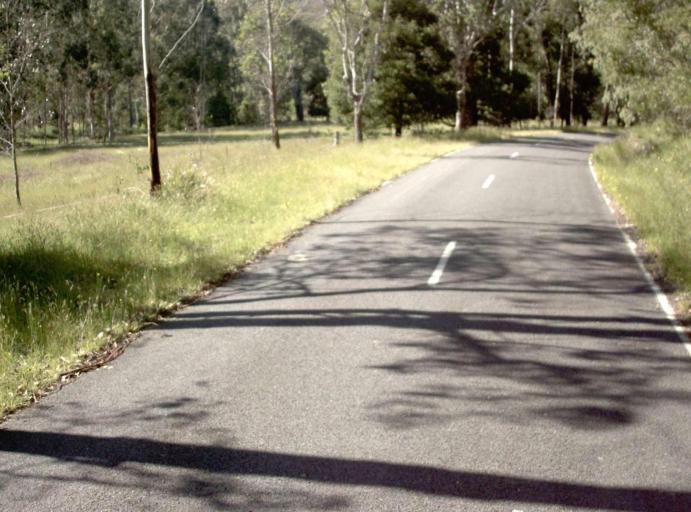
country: AU
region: New South Wales
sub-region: Bombala
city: Bombala
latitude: -37.3682
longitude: 148.6826
